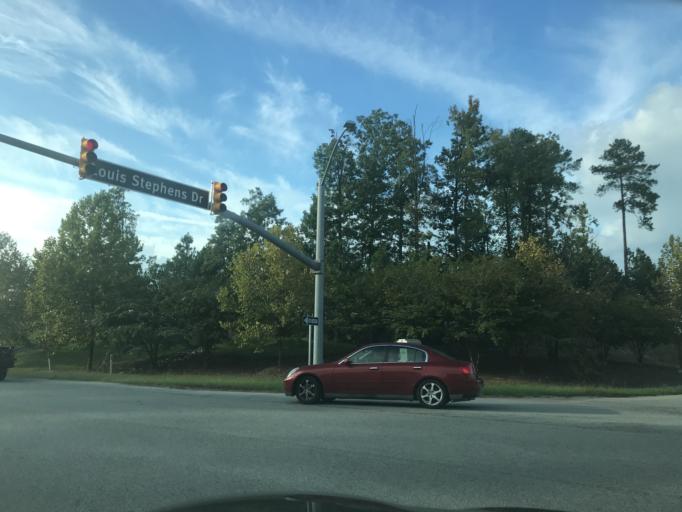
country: US
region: North Carolina
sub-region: Wake County
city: Morrisville
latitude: 35.8598
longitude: -78.8865
